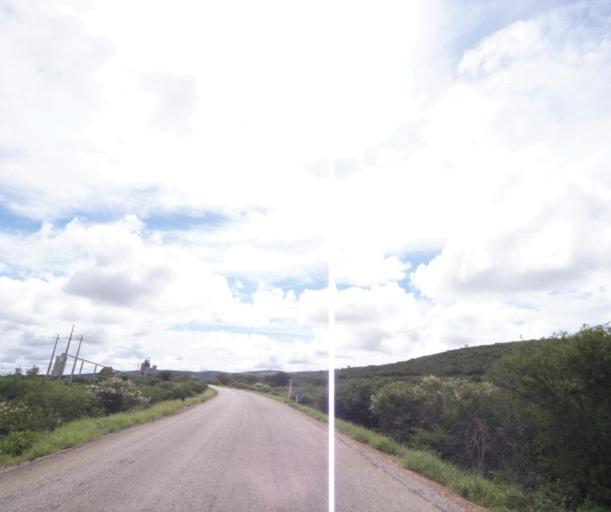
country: BR
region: Bahia
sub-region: Brumado
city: Brumado
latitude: -14.2002
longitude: -41.6051
